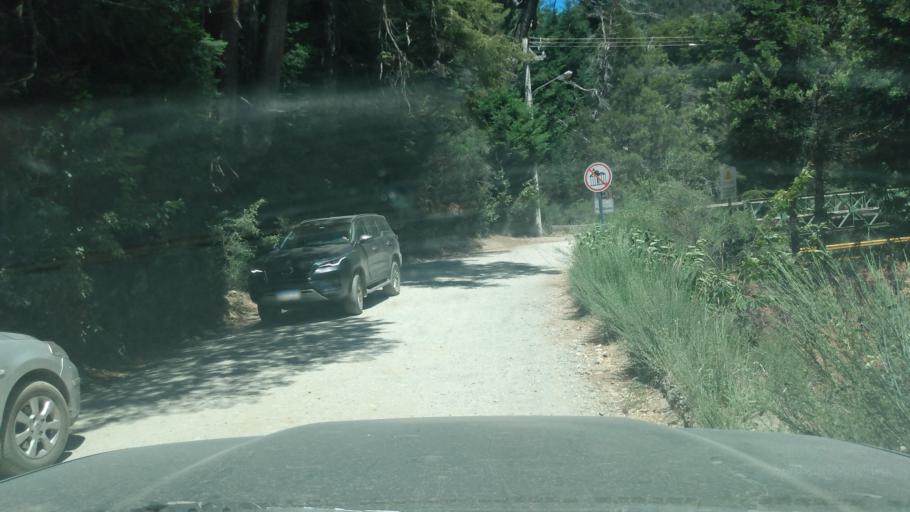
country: AR
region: Rio Negro
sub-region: Departamento de Bariloche
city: San Carlos de Bariloche
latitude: -41.0969
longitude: -71.5181
